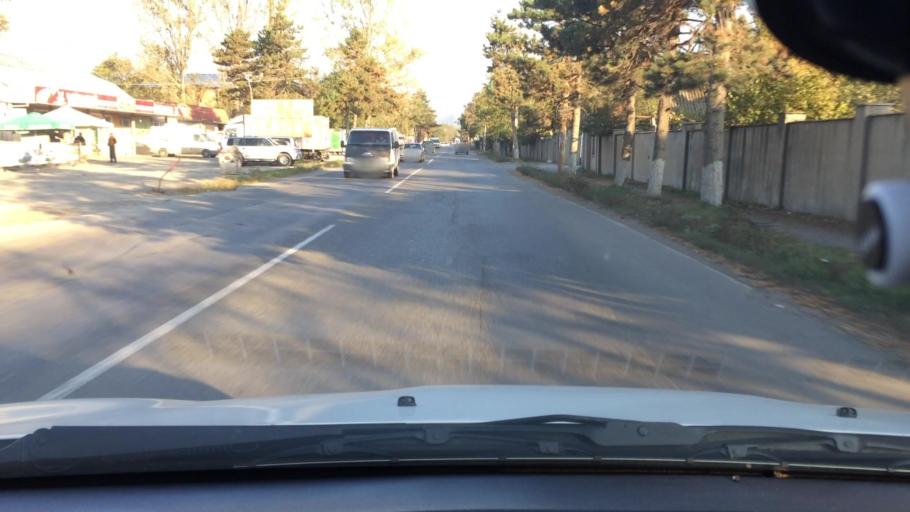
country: GE
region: Shida Kartli
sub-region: Khashuris Raioni
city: Khashuri
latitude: 41.9891
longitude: 43.5918
